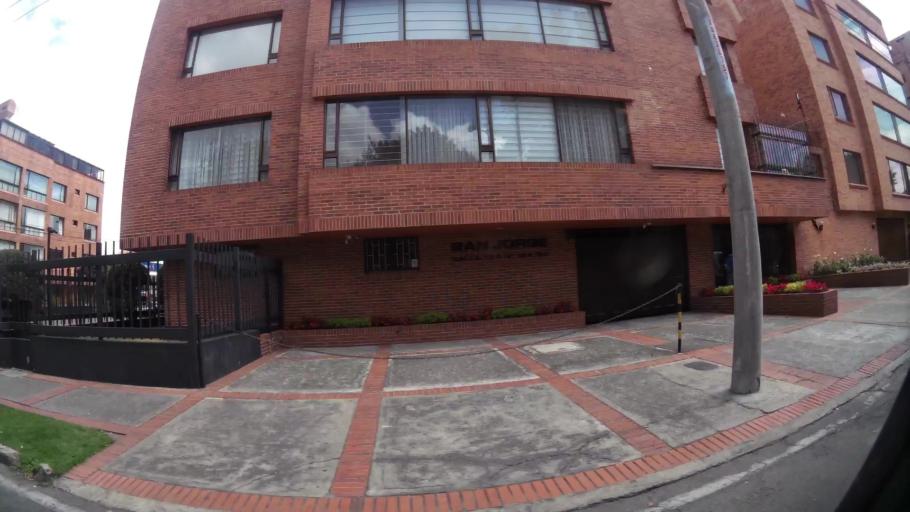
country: CO
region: Bogota D.C.
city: Barrio San Luis
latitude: 4.7040
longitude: -74.0506
